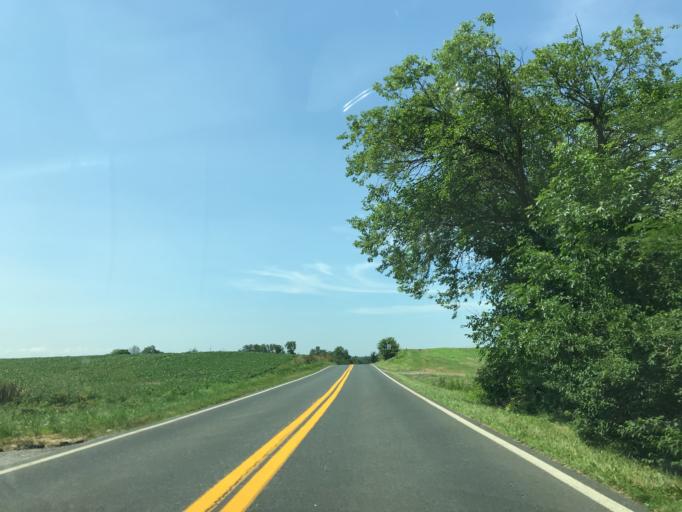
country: US
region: Maryland
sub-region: Carroll County
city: Taneytown
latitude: 39.6197
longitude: -77.1381
